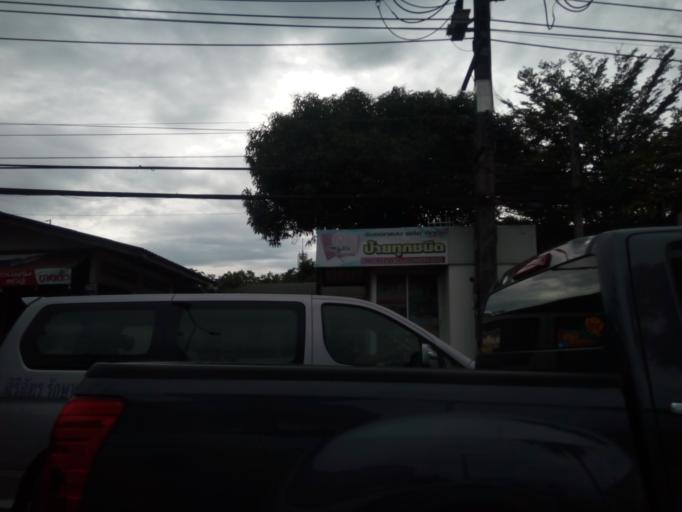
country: TH
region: Phuket
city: Thalang
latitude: 8.0215
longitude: 98.3351
